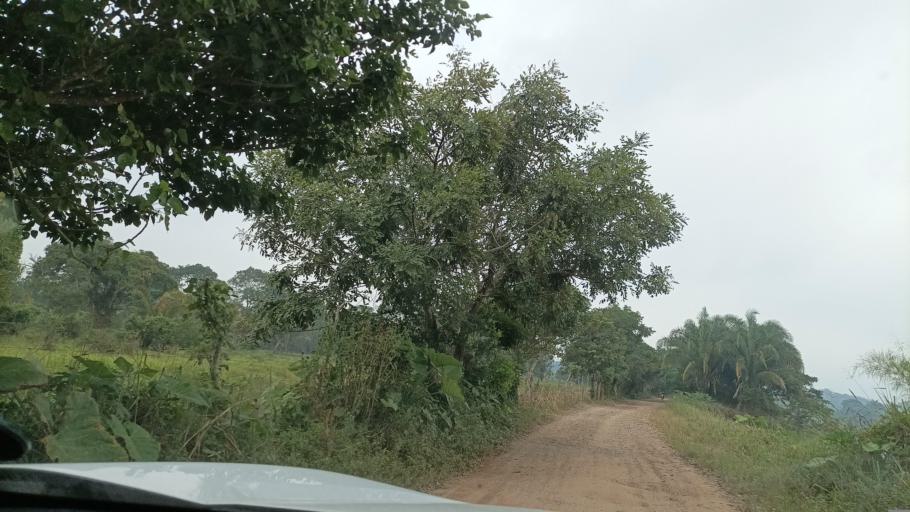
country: MX
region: Veracruz
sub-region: Uxpanapa
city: Poblado 10
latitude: 17.5602
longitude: -94.2254
